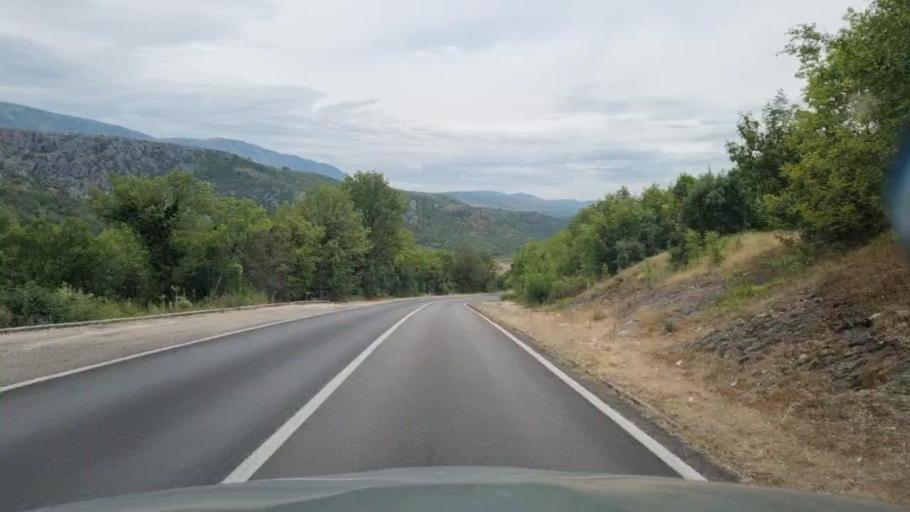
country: BA
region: Federation of Bosnia and Herzegovina
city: Stolac
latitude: 43.0998
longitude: 17.9098
